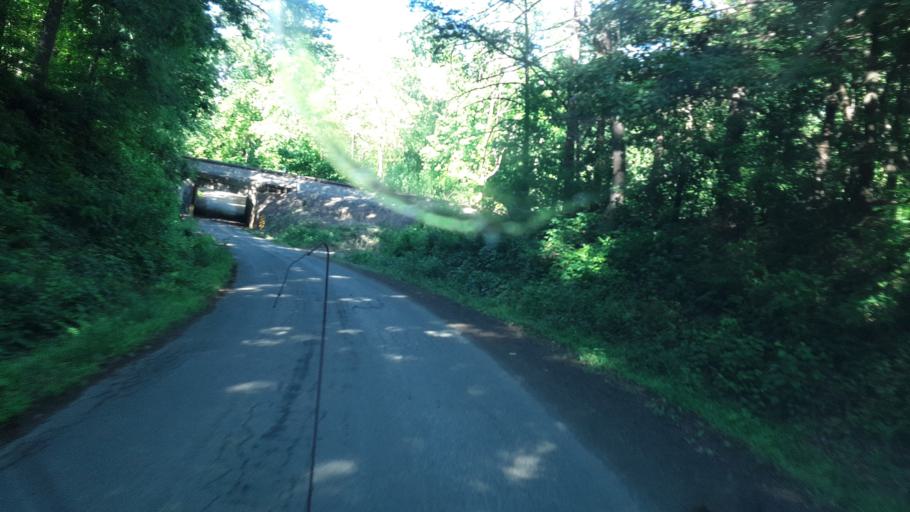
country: US
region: Virginia
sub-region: Pittsylvania County
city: Chatham
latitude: 36.8391
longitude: -79.4097
